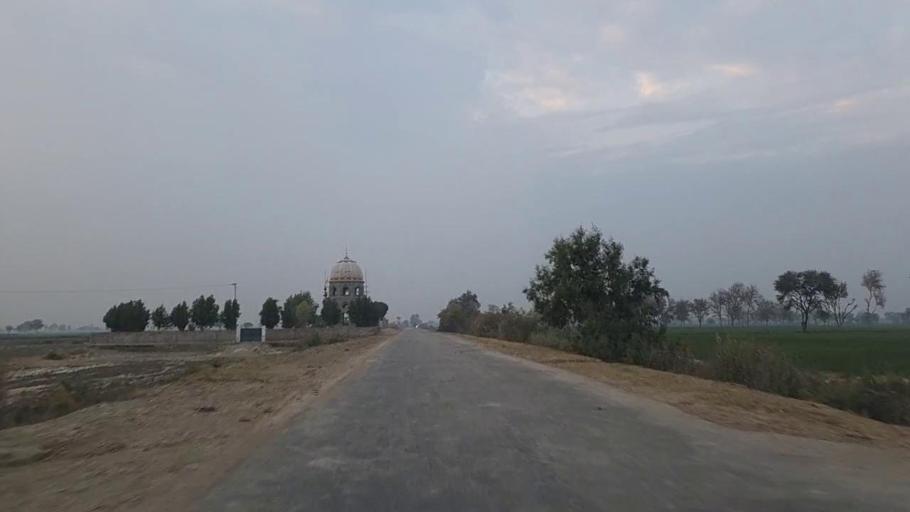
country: PK
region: Sindh
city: Jam Sahib
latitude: 26.3173
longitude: 68.5671
